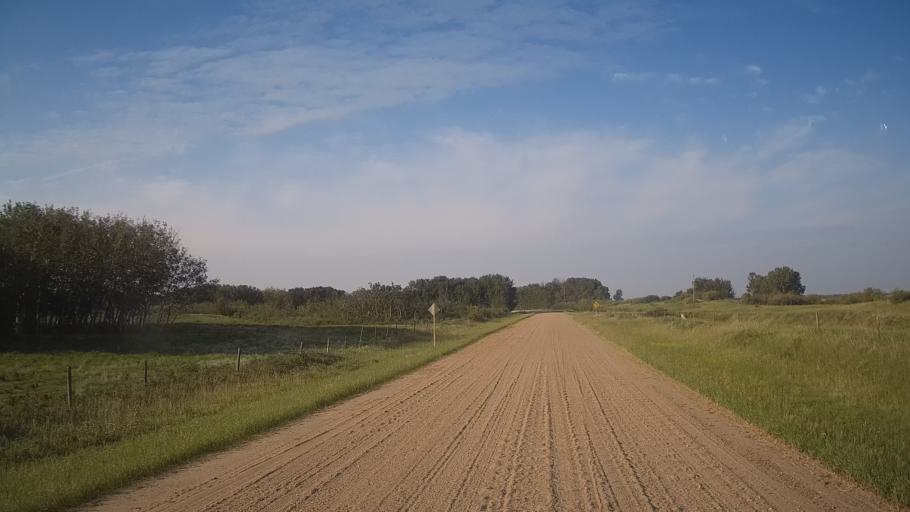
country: CA
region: Saskatchewan
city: Saskatoon
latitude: 51.8274
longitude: -106.5419
